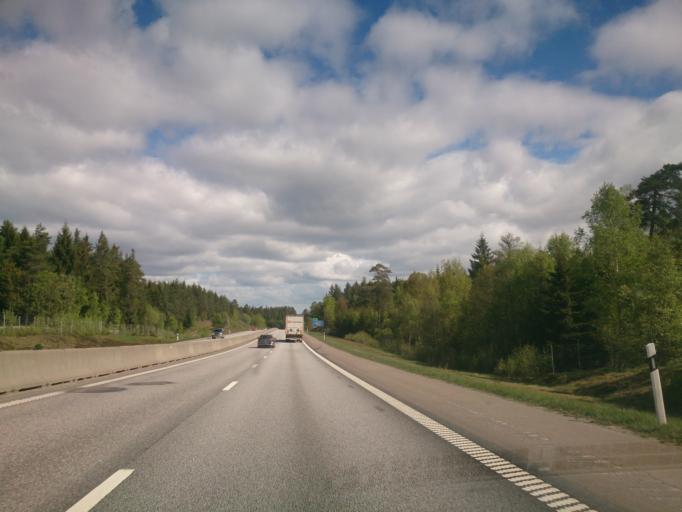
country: SE
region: OEstergoetland
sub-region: Norrkopings Kommun
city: Kimstad
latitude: 58.5407
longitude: 16.0421
